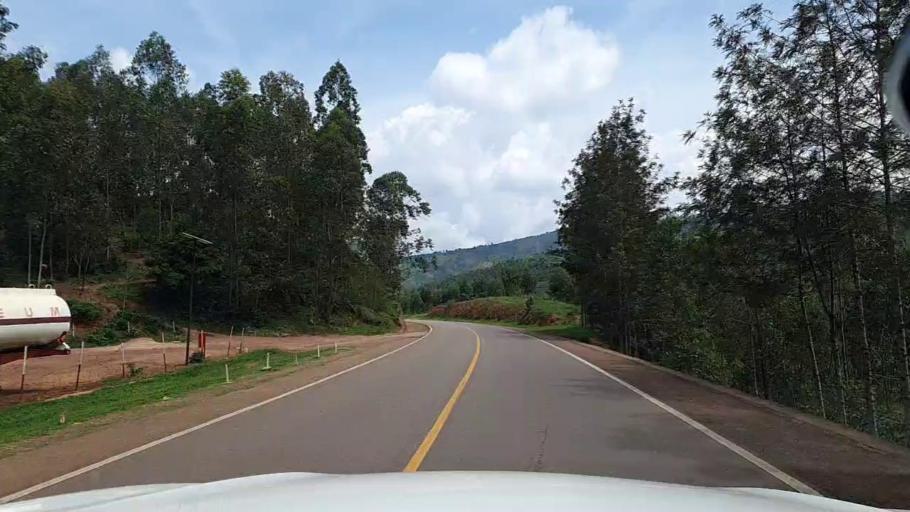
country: RW
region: Kigali
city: Kigali
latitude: -1.8572
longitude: 30.0961
